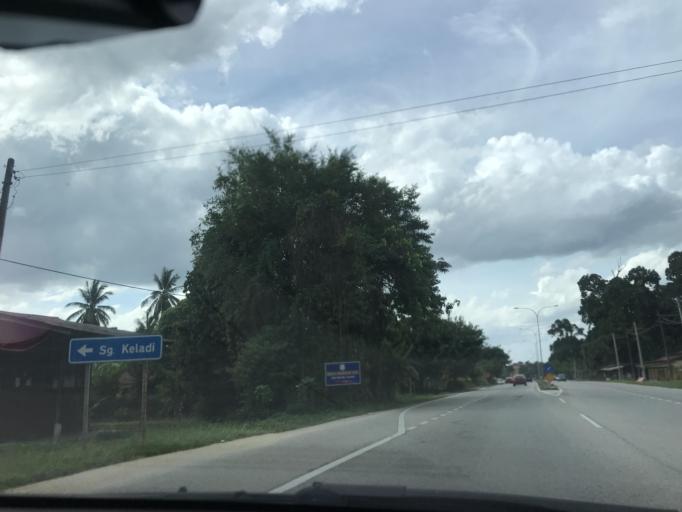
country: MY
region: Kelantan
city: Kampong Pangkal Kalong
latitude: 5.9174
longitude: 102.1882
